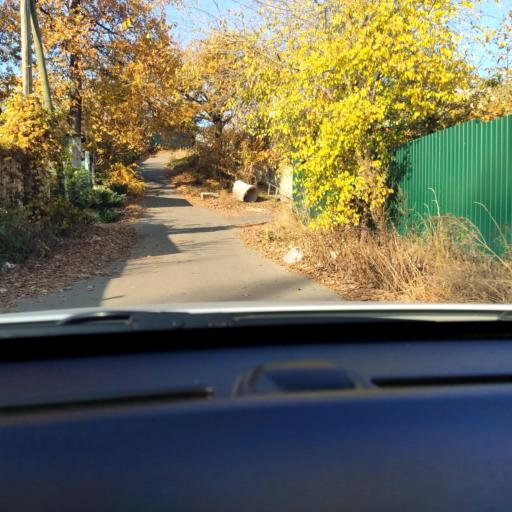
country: RU
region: Voronezj
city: Voronezh
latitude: 51.7074
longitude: 39.2389
